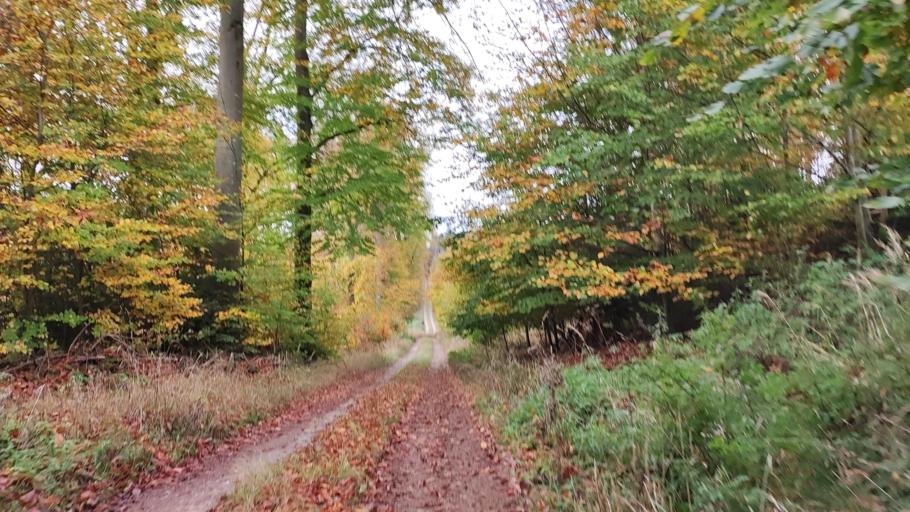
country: DE
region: Bavaria
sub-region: Swabia
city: Ziemetshausen
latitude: 48.3429
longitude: 10.5263
